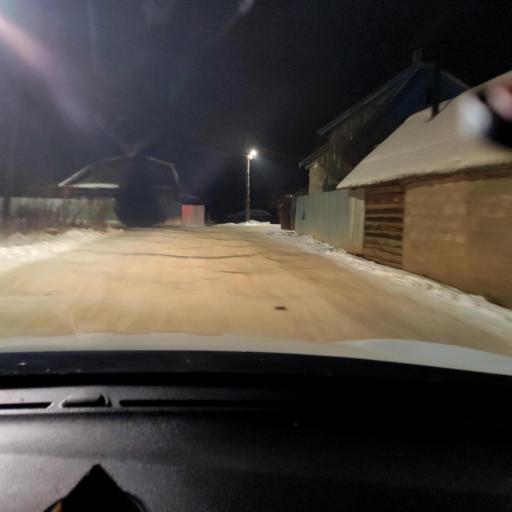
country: RU
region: Tatarstan
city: Stolbishchi
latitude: 55.6471
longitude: 49.2084
